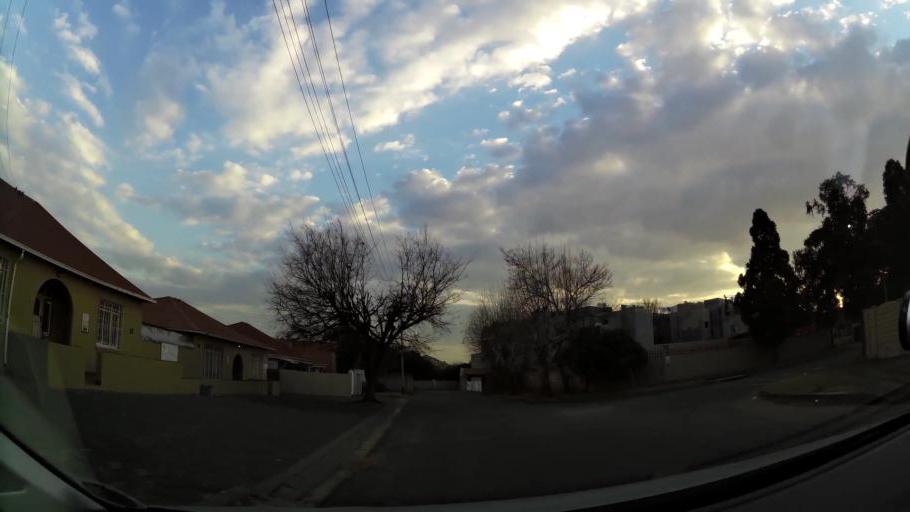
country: ZA
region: Gauteng
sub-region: Ekurhuleni Metropolitan Municipality
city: Germiston
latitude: -26.1917
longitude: 28.1589
